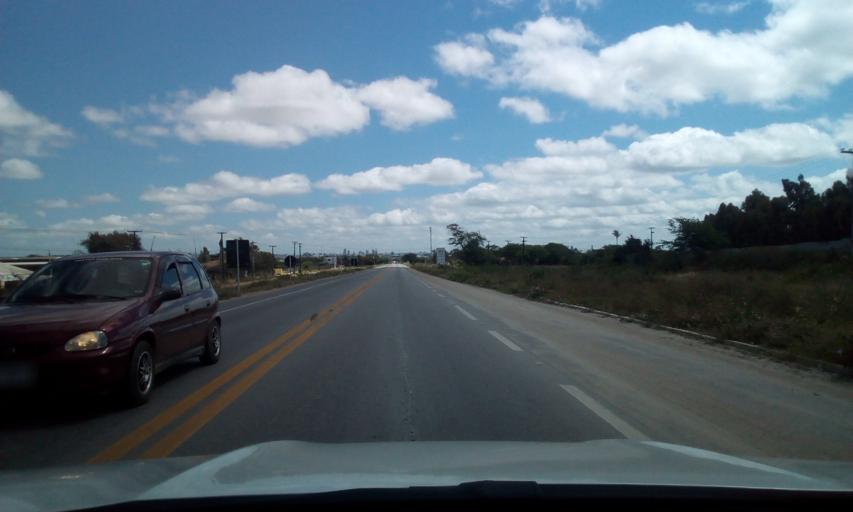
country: BR
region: Paraiba
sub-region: Campina Grande
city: Campina Grande
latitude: -7.3021
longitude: -35.8924
